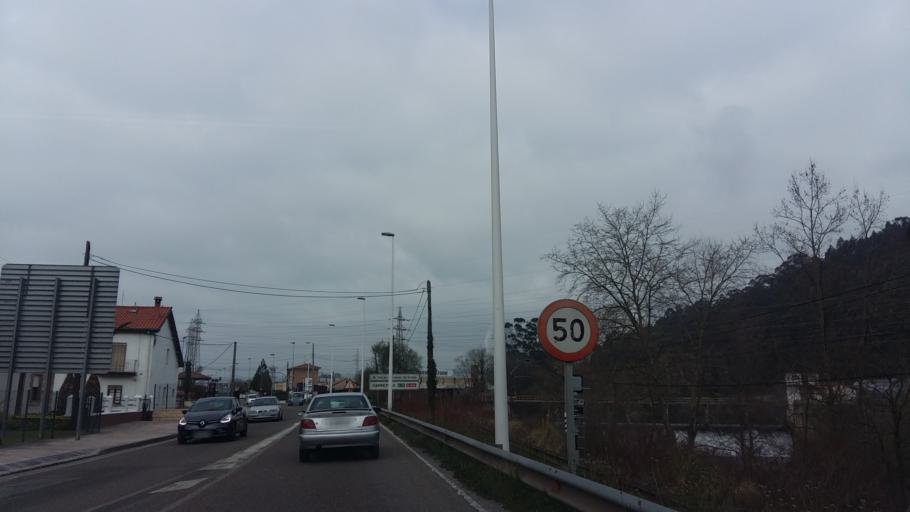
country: ES
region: Cantabria
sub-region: Provincia de Cantabria
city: Reocin
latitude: 43.3575
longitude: -4.0745
